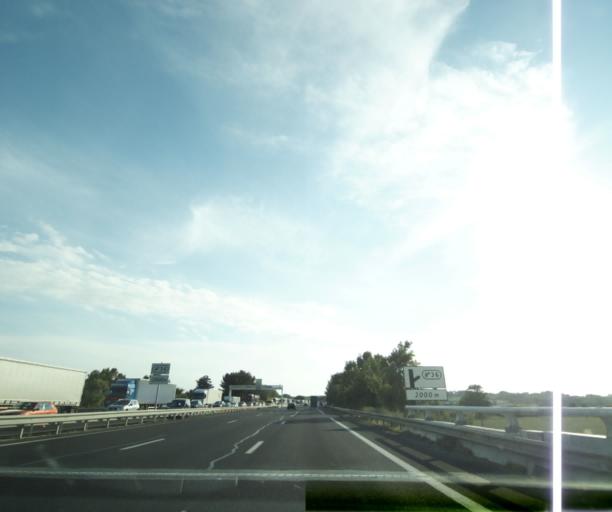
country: FR
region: Languedoc-Roussillon
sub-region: Departement de l'Herault
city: Sauvian
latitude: 43.3098
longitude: 3.2488
